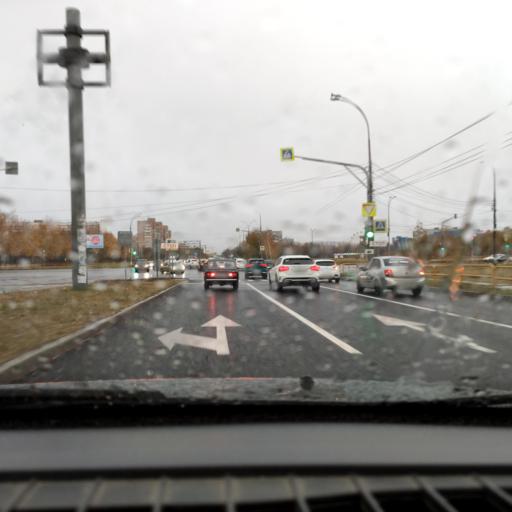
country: RU
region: Samara
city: Tol'yatti
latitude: 53.5149
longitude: 49.2794
